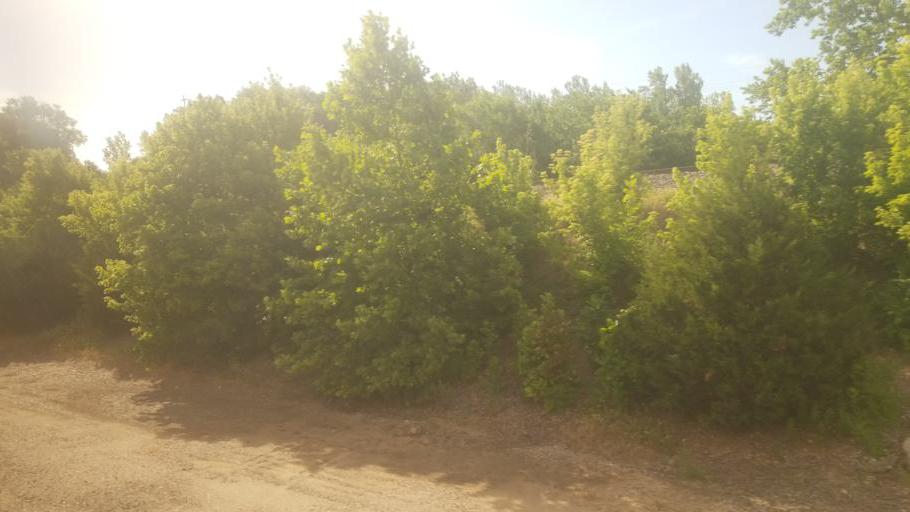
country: US
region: Kansas
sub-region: Wyandotte County
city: Edwardsville
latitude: 39.0407
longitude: -94.8026
